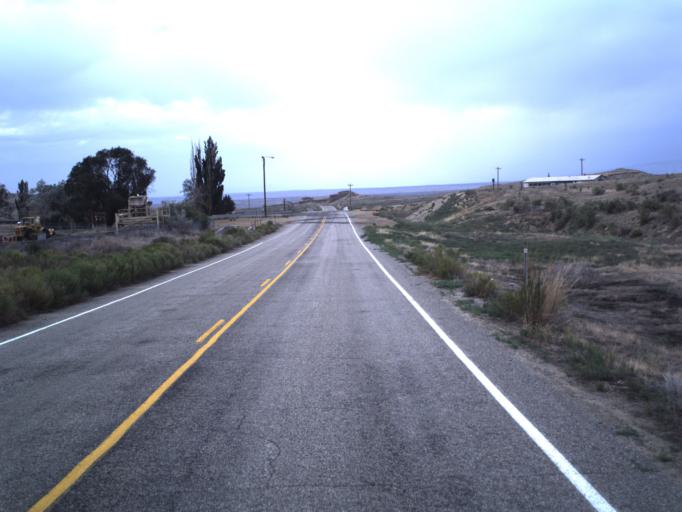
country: US
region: Colorado
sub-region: Rio Blanco County
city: Rangely
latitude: 40.0175
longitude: -109.1723
